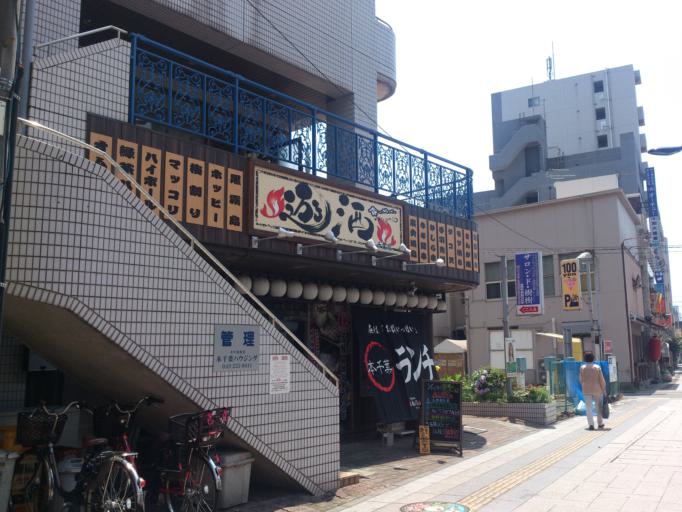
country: JP
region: Chiba
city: Chiba
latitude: 35.6031
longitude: 140.1221
